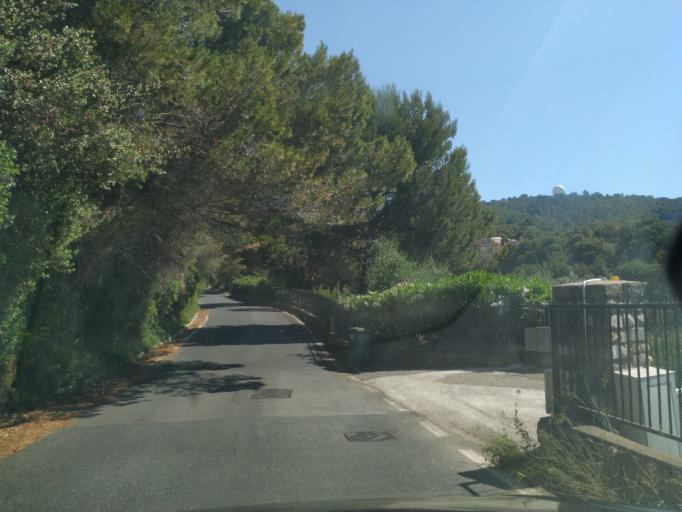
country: IT
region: Liguria
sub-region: Provincia di Savona
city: Marina di Andora
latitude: 43.9544
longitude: 8.1589
